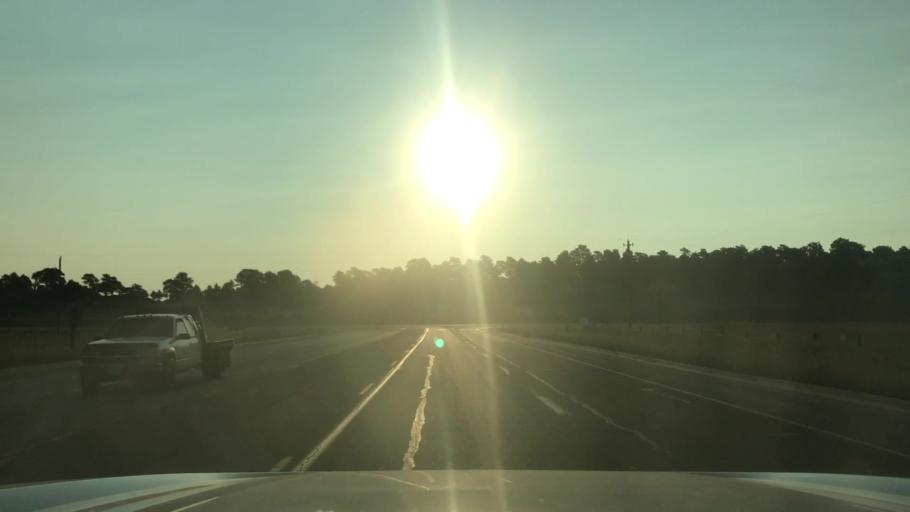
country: US
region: Wyoming
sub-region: Natrona County
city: Evansville
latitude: 42.8399
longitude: -106.2187
